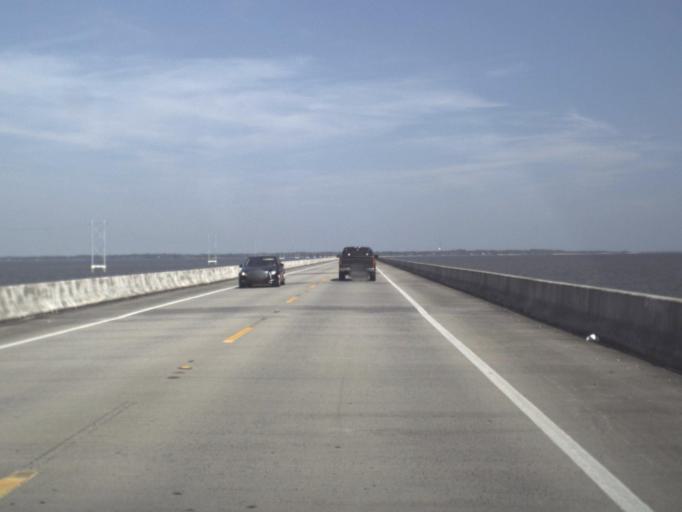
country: US
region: Florida
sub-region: Franklin County
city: Apalachicola
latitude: 29.7287
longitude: -84.9501
